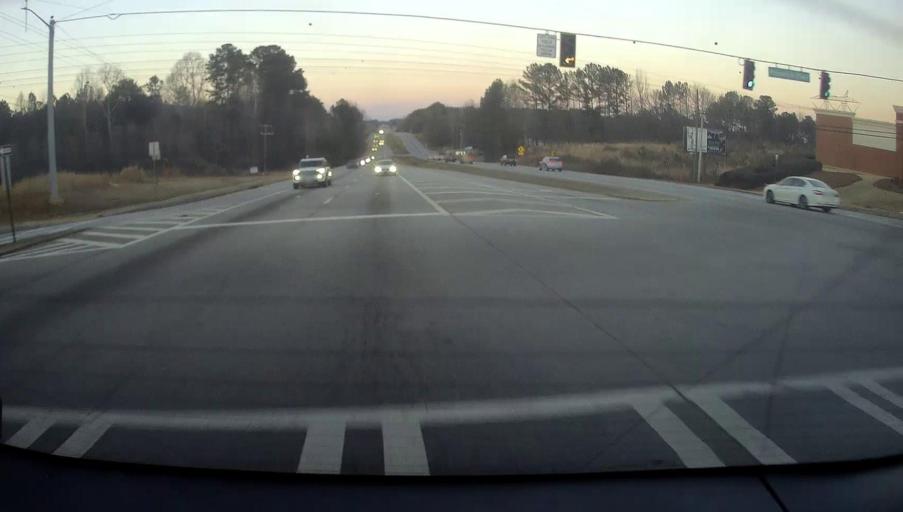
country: US
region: Georgia
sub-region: Fayette County
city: Fayetteville
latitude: 33.4828
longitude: -84.4353
